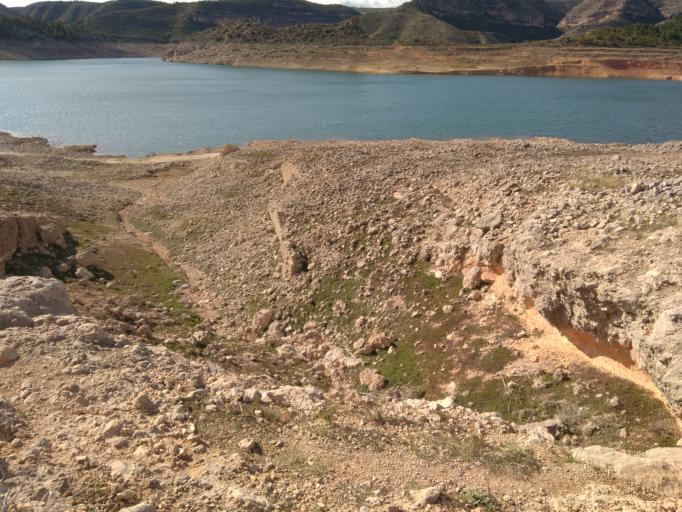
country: ES
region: Valencia
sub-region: Provincia de Valencia
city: Sumacarcer
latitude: 39.1565
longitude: -0.6593
